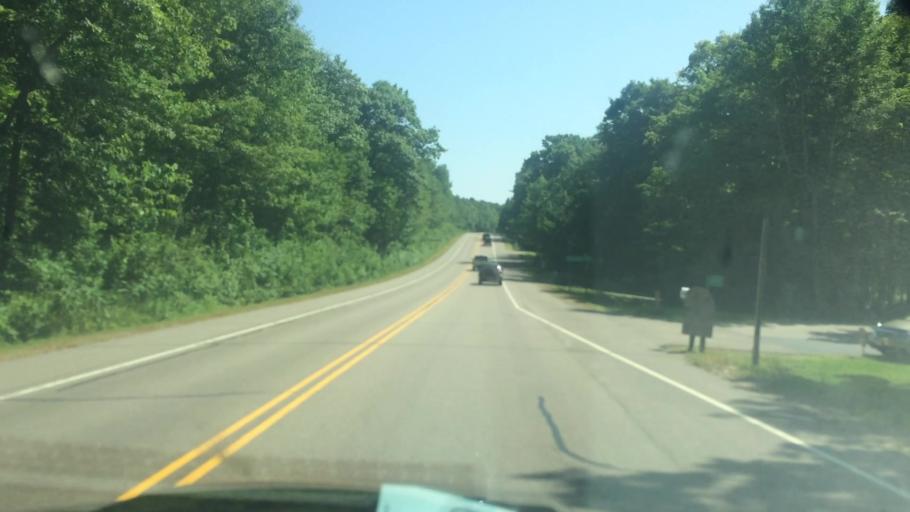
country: US
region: Wisconsin
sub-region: Oneida County
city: Rhinelander
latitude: 45.6156
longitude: -89.5305
